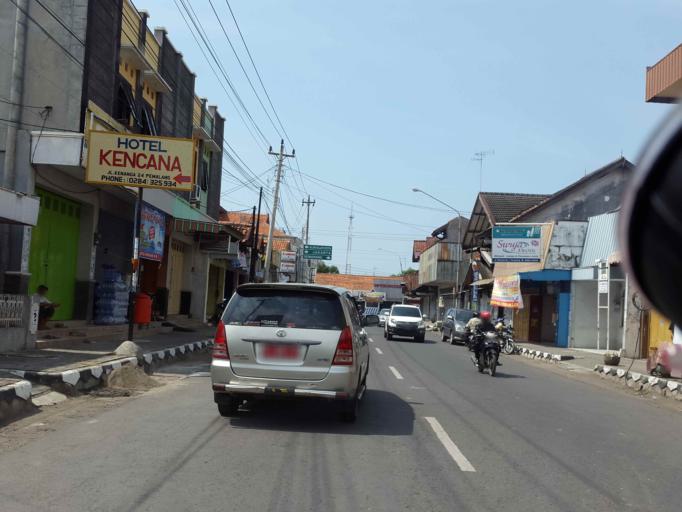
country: ID
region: Central Java
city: Pemalang
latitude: -6.8912
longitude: 109.3885
